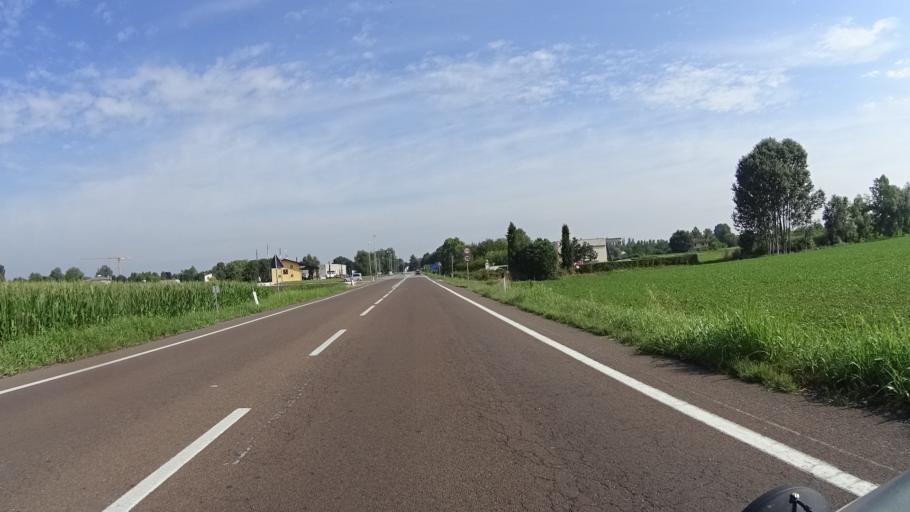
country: IT
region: Veneto
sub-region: Provincia di Venezia
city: San Michele al Tagliamento
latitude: 45.7651
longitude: 12.9852
